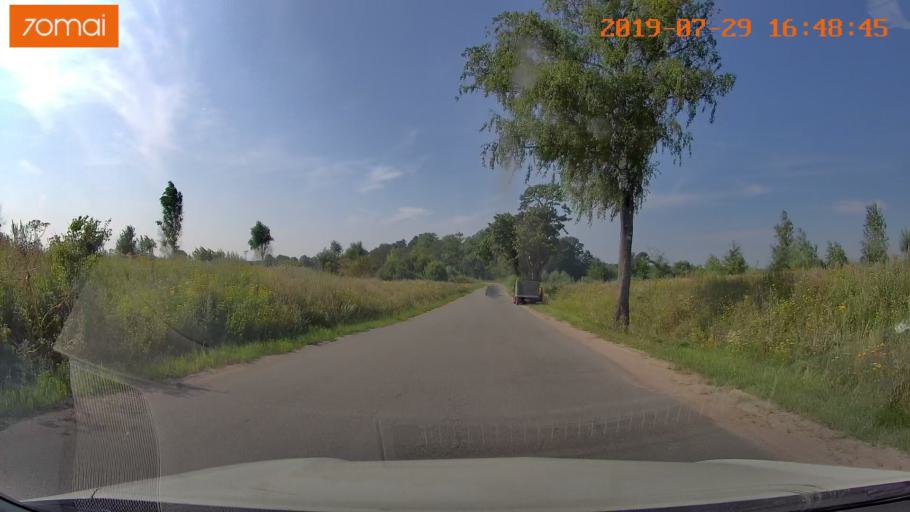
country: RU
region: Kaliningrad
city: Primorsk
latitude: 54.7891
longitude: 20.0735
